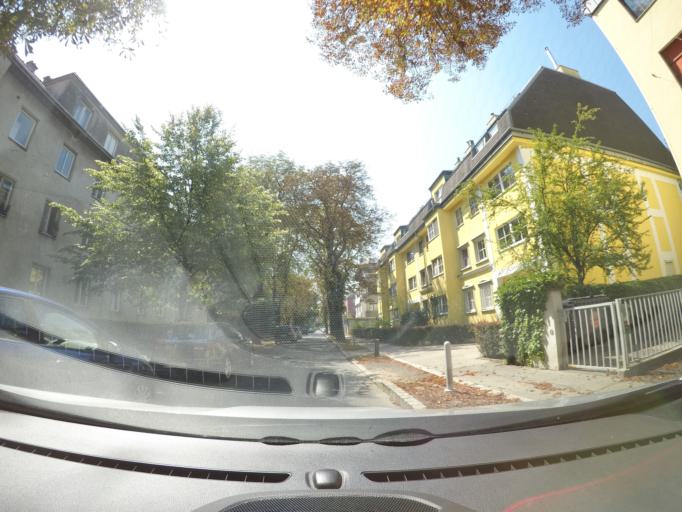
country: AT
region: Lower Austria
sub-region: Politischer Bezirk Modling
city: Perchtoldsdorf
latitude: 48.1884
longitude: 16.2799
